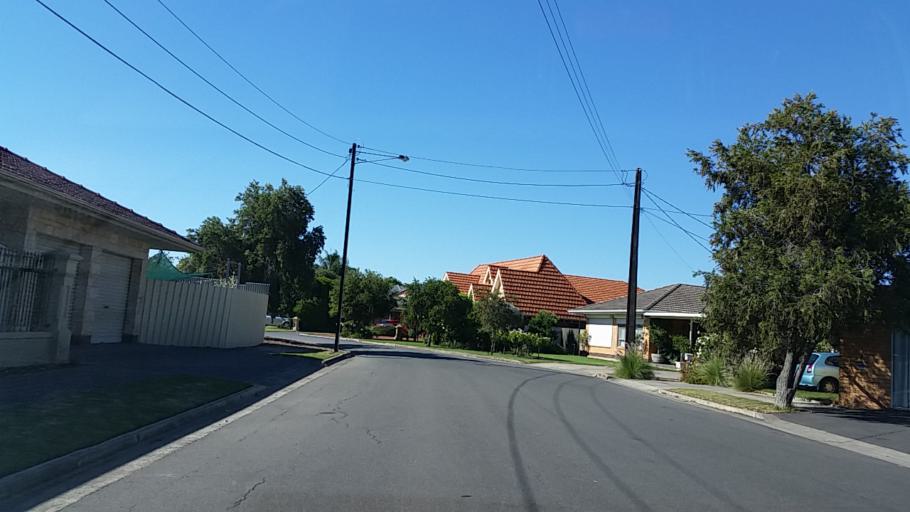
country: AU
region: South Australia
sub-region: Charles Sturt
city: Henley Beach
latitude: -34.9220
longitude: 138.5106
